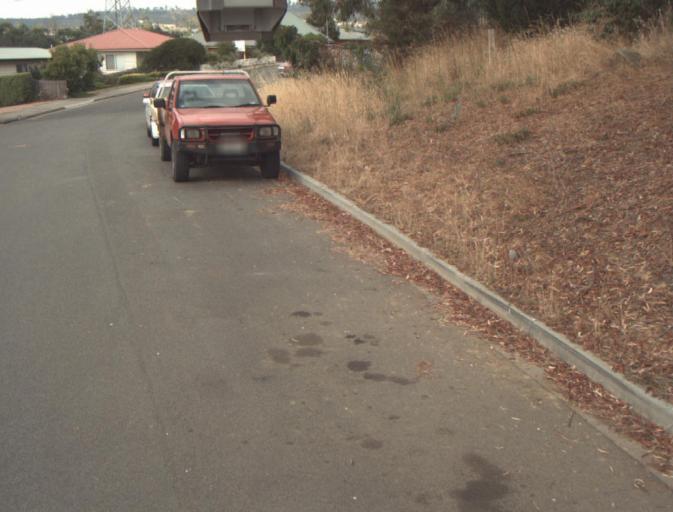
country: AU
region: Tasmania
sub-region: Launceston
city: Summerhill
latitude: -41.4824
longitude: 147.1747
